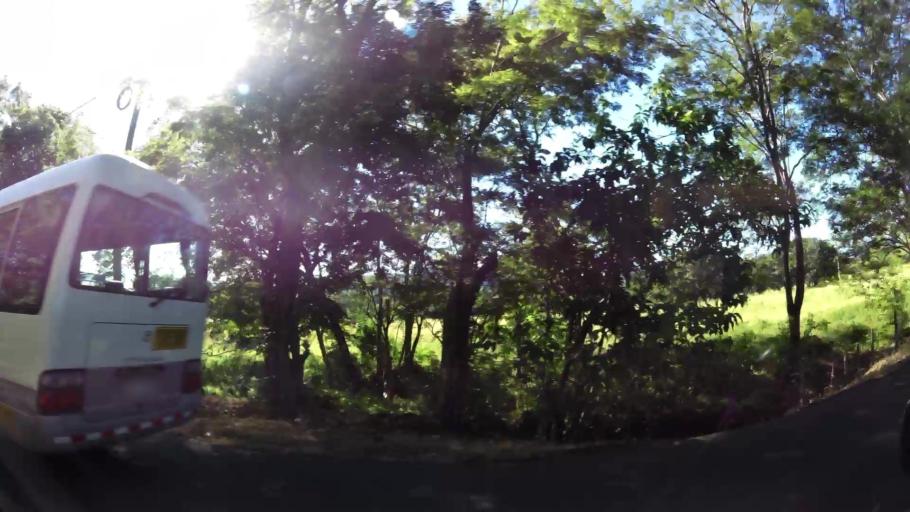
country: CR
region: Guanacaste
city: Belen
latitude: 10.3973
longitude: -85.6094
